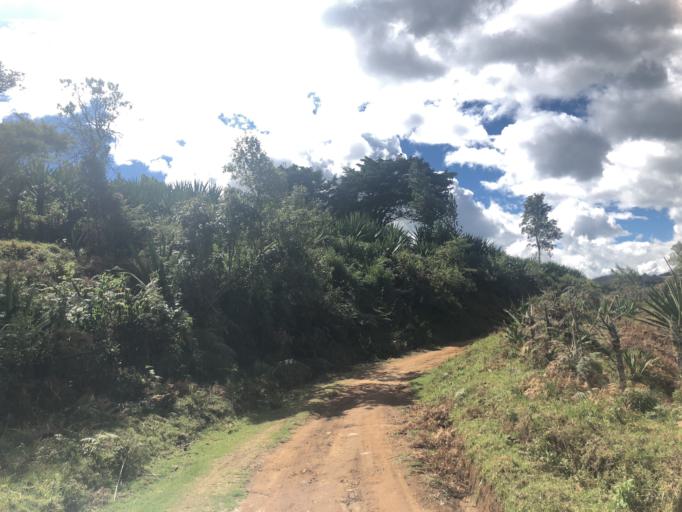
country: CO
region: Cauca
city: Silvia
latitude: 2.6783
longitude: -76.4421
